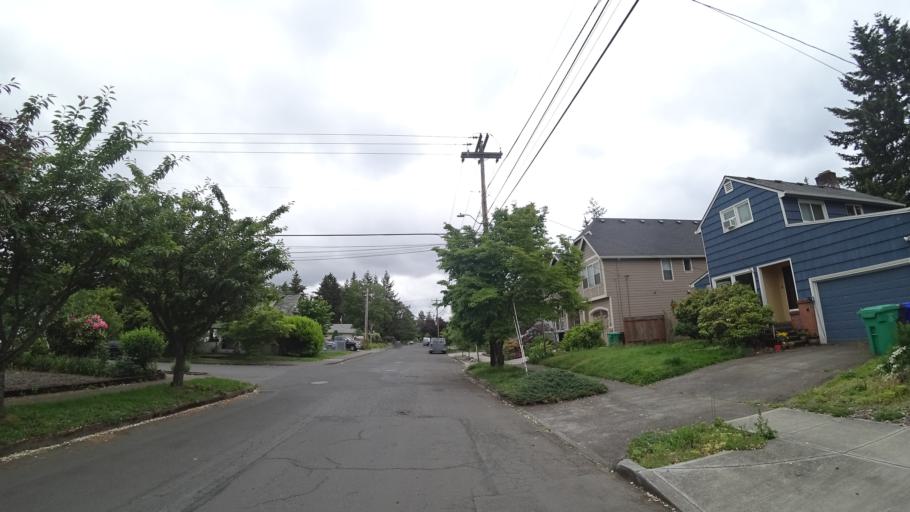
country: US
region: Oregon
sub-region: Multnomah County
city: Lents
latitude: 45.4854
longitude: -122.6044
